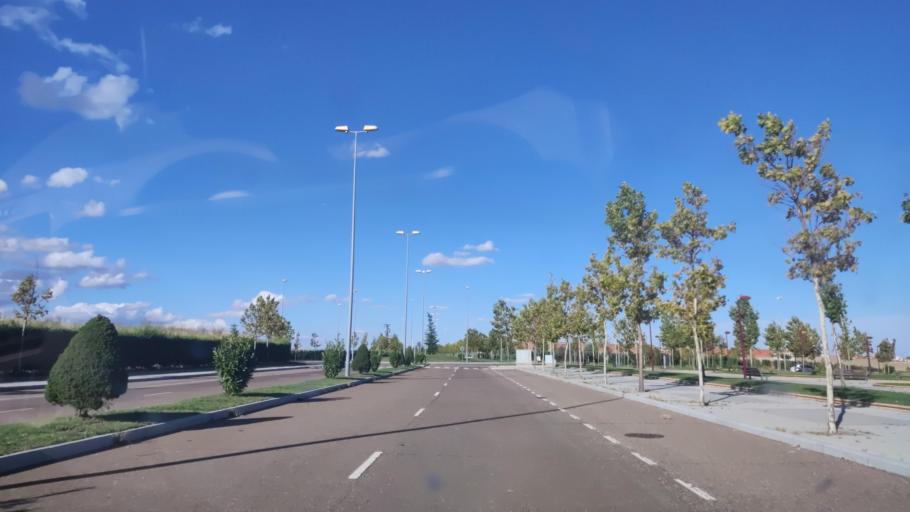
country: ES
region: Castille and Leon
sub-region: Provincia de Salamanca
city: Salamanca
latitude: 40.9721
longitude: -5.6895
